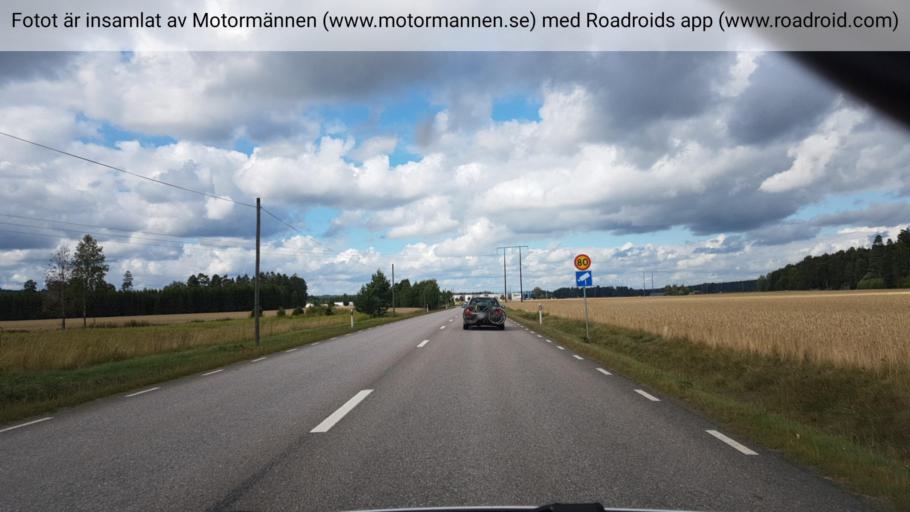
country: SE
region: Vaestra Goetaland
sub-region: Ulricehamns Kommun
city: Ulricehamn
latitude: 57.8364
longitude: 13.4382
